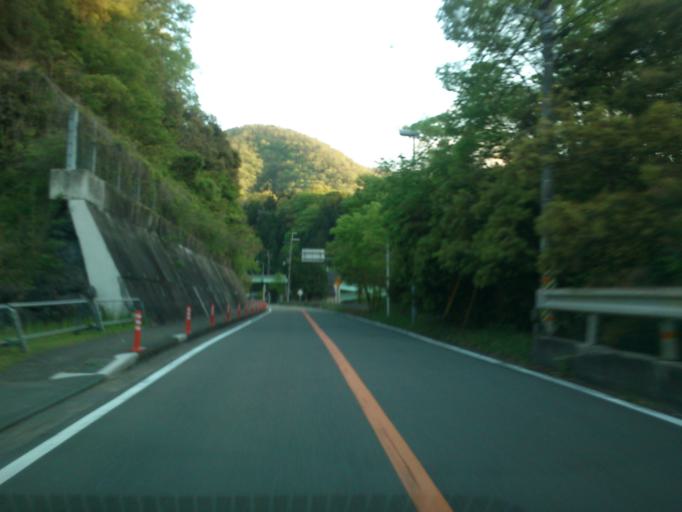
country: JP
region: Kyoto
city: Ayabe
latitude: 35.2187
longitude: 135.4199
